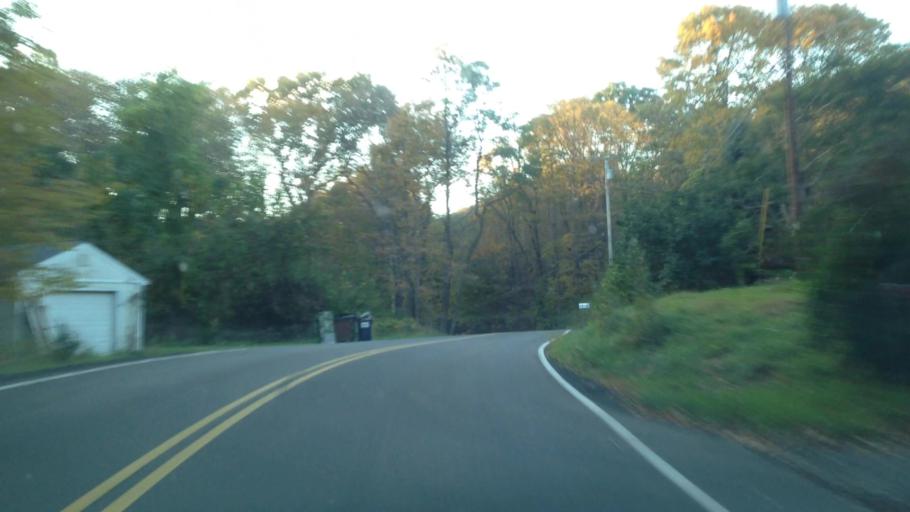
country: US
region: New York
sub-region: Ulster County
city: Tillson
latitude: 41.8249
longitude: -74.0042
